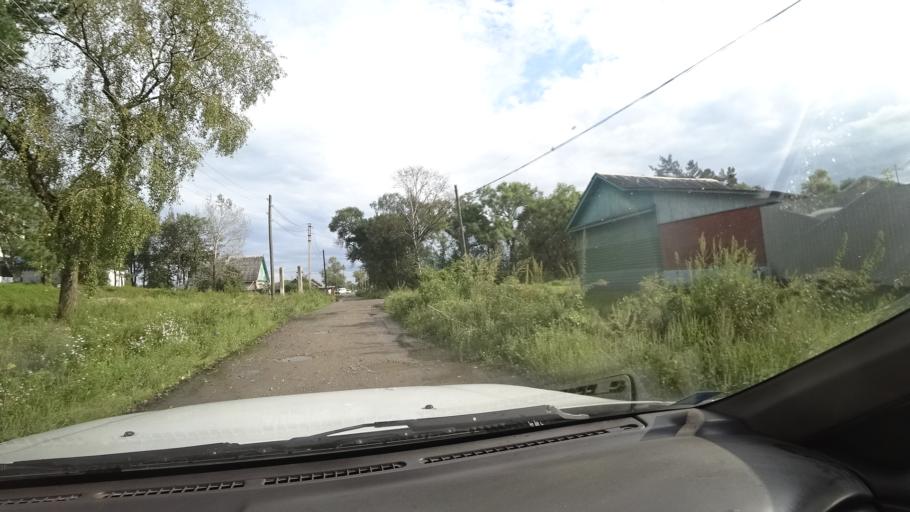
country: RU
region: Primorskiy
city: Dal'nerechensk
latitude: 45.9352
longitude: 133.7463
